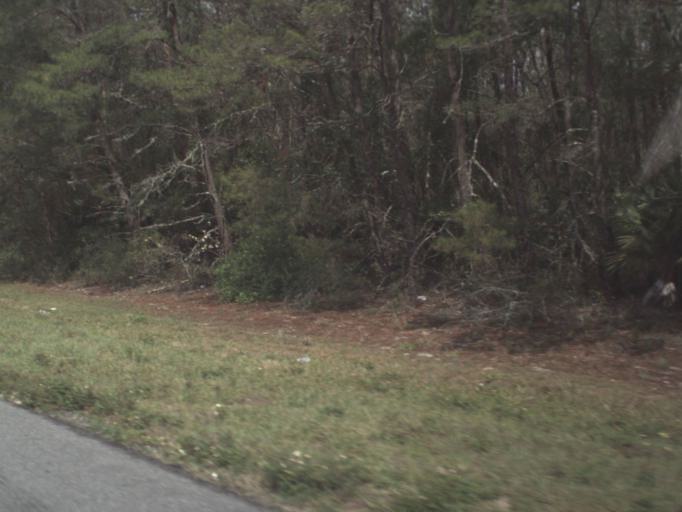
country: US
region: Florida
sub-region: Lake County
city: Astor
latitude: 29.1714
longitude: -81.6253
